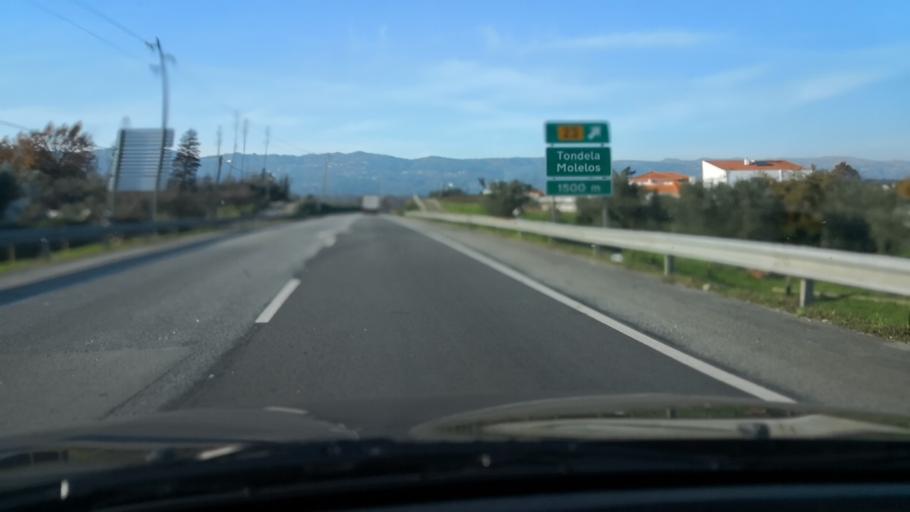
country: PT
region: Viseu
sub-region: Concelho de Tondela
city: Tondela
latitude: 40.5136
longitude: -8.0904
